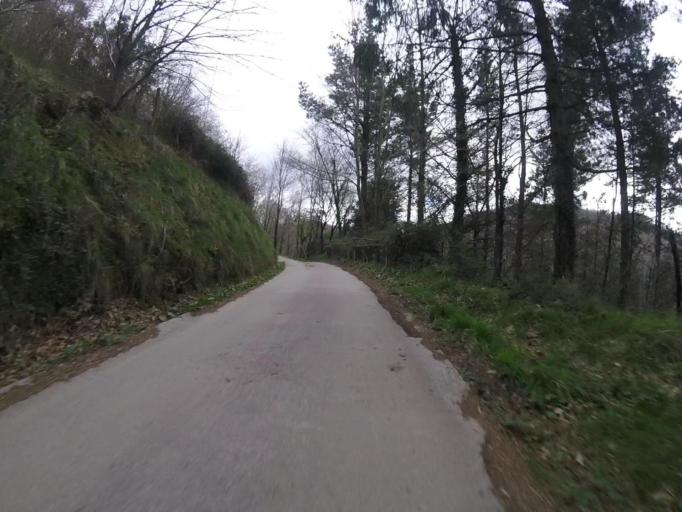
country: ES
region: Basque Country
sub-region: Provincia de Guipuzcoa
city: Errenteria
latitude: 43.2732
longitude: -1.8602
